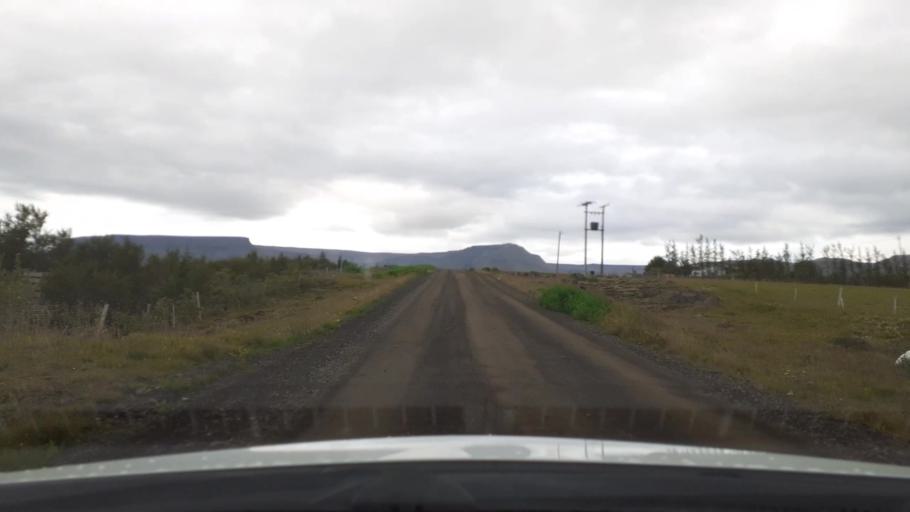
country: IS
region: Capital Region
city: Mosfellsbaer
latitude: 64.1899
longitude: -21.5383
